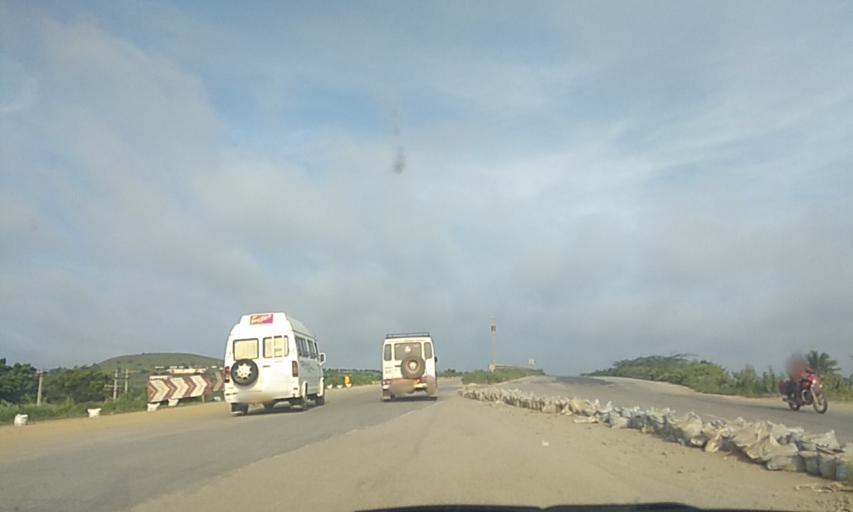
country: IN
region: Karnataka
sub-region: Haveri
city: Haveri
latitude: 14.7619
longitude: 75.4361
